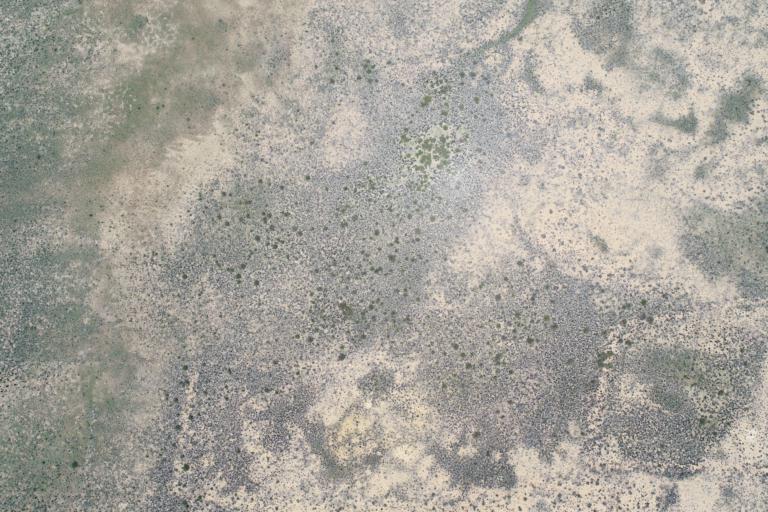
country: BO
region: La Paz
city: Curahuara de Carangas
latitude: -17.3080
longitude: -68.5129
